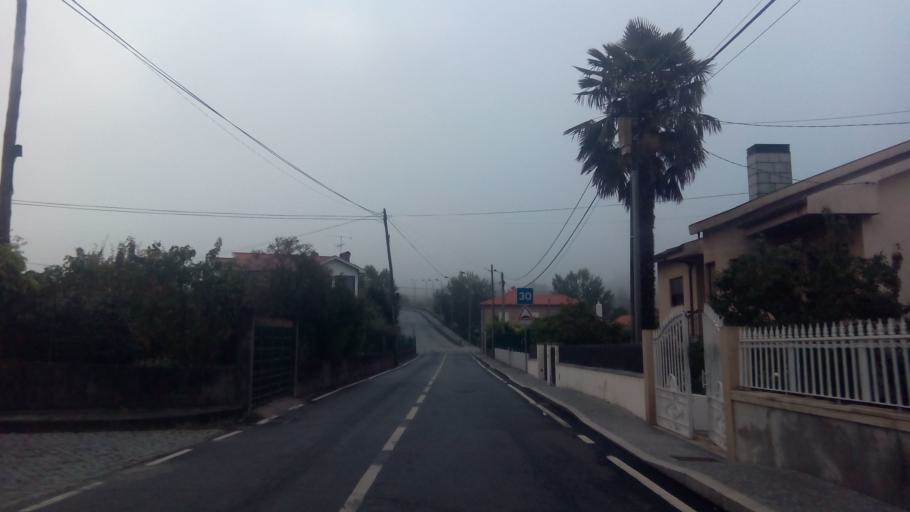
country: PT
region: Porto
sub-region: Penafiel
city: Penafiel
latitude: 41.2142
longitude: -8.3013
